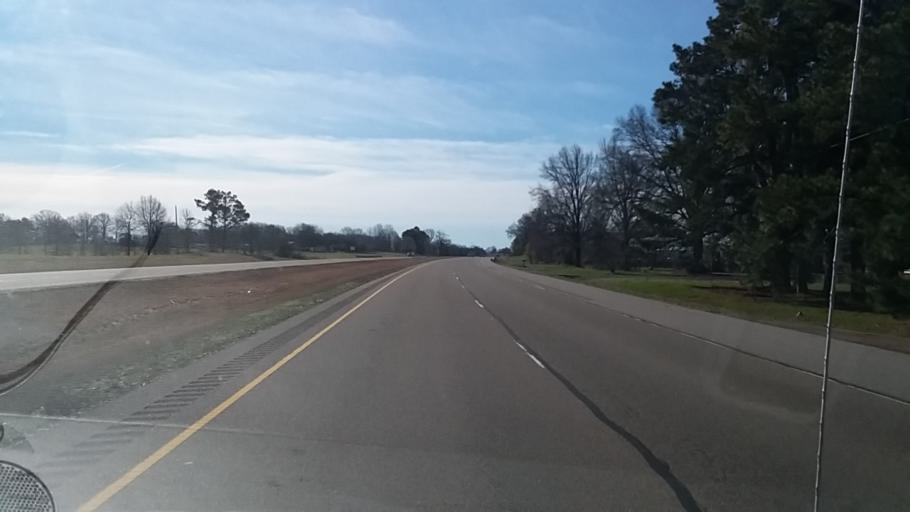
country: US
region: Tennessee
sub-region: Crockett County
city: Alamo
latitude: 35.8515
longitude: -89.1967
